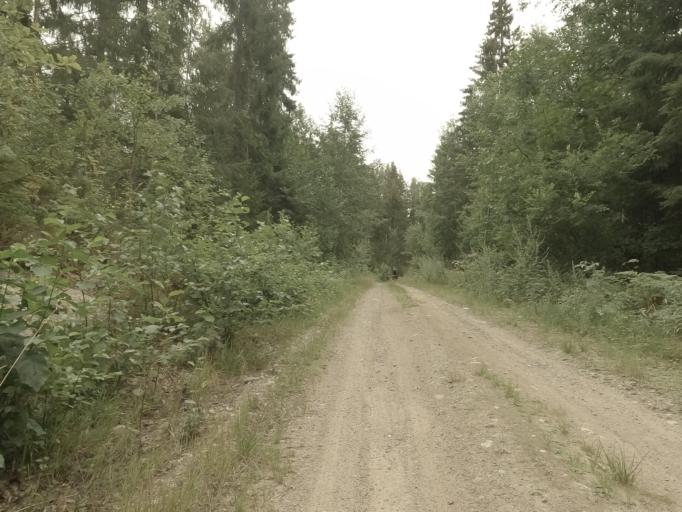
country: RU
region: Leningrad
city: Kamennogorsk
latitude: 61.0687
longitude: 29.1665
